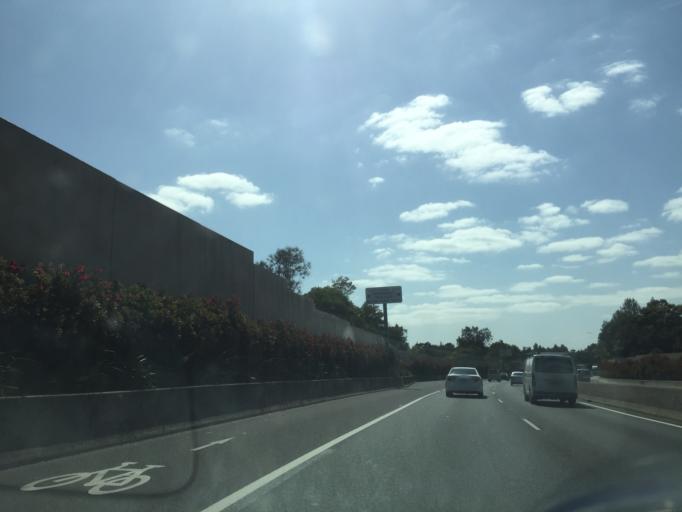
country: AU
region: New South Wales
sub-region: Canterbury
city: Clemton Park
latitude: -33.9407
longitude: 151.0836
